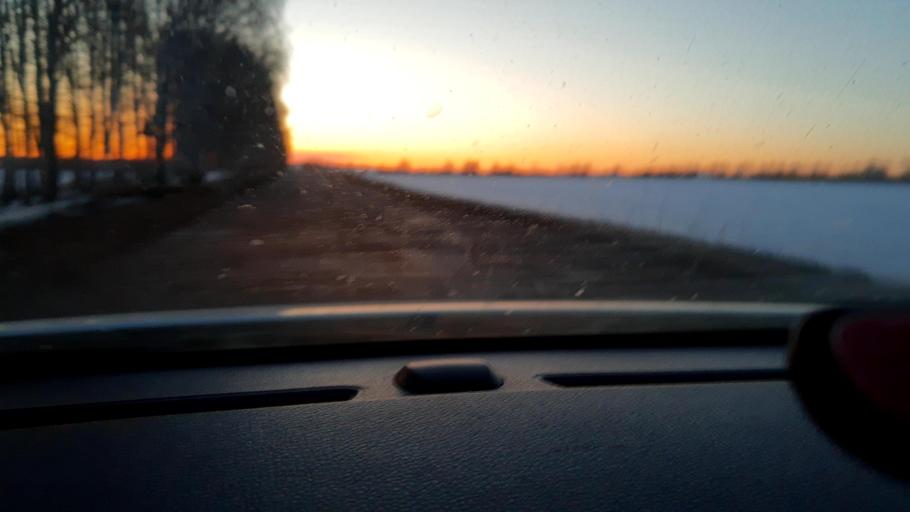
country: RU
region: Bashkortostan
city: Avdon
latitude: 54.3878
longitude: 55.7462
